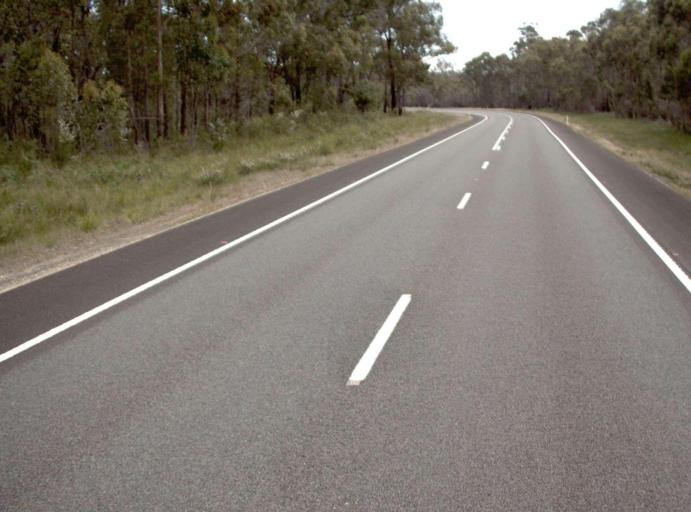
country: AU
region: New South Wales
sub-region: Bega Valley
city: Eden
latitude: -37.5162
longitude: 149.5002
